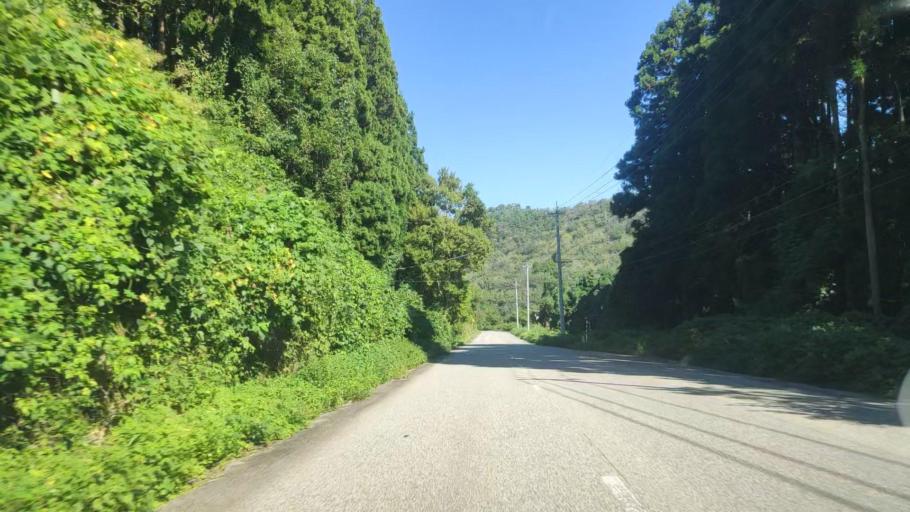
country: JP
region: Ishikawa
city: Nanao
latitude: 37.2134
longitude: 136.7067
